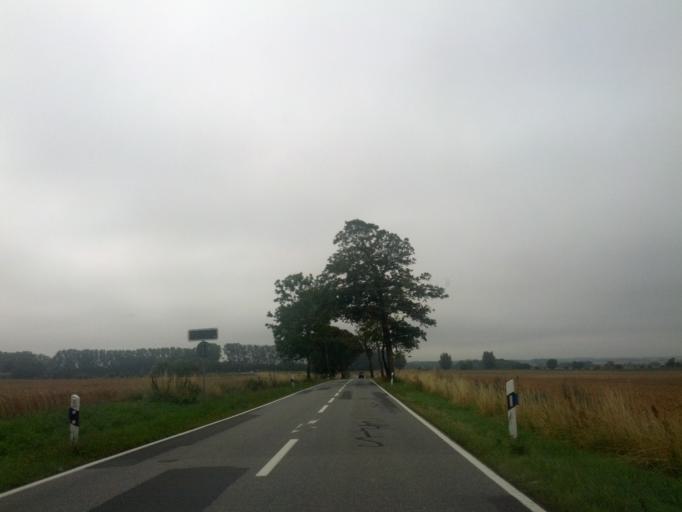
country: DE
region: Mecklenburg-Vorpommern
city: Bastorf
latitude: 54.1033
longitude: 11.6781
